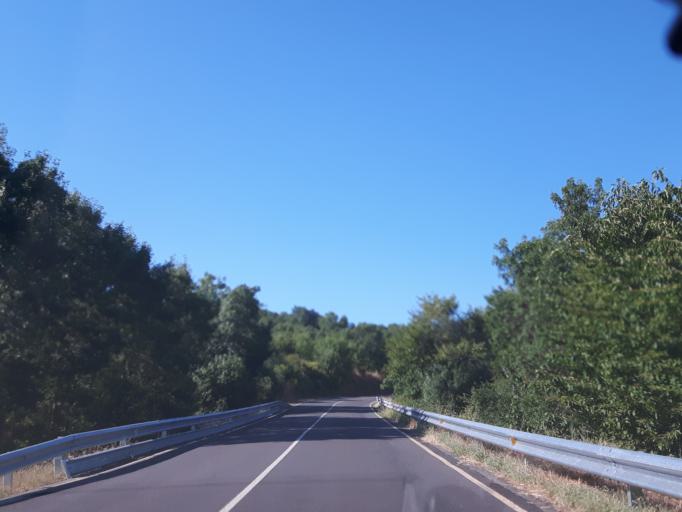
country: ES
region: Castille and Leon
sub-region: Provincia de Salamanca
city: Navalmoral de Bejar
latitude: 40.4089
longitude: -5.8098
